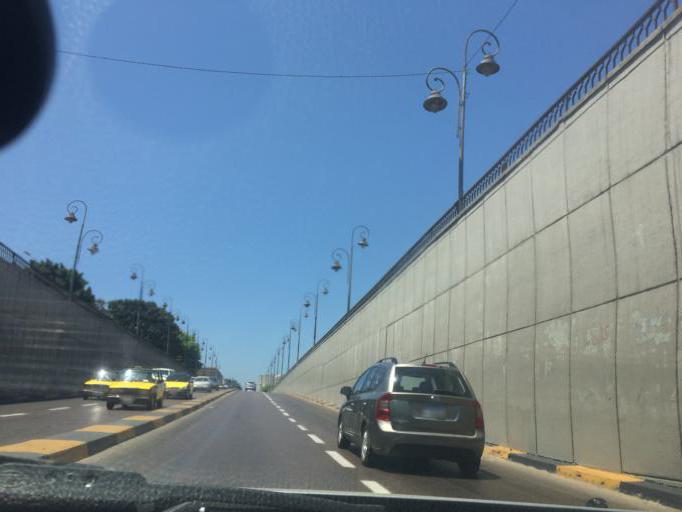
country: EG
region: Alexandria
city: Alexandria
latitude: 31.2023
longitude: 29.9158
